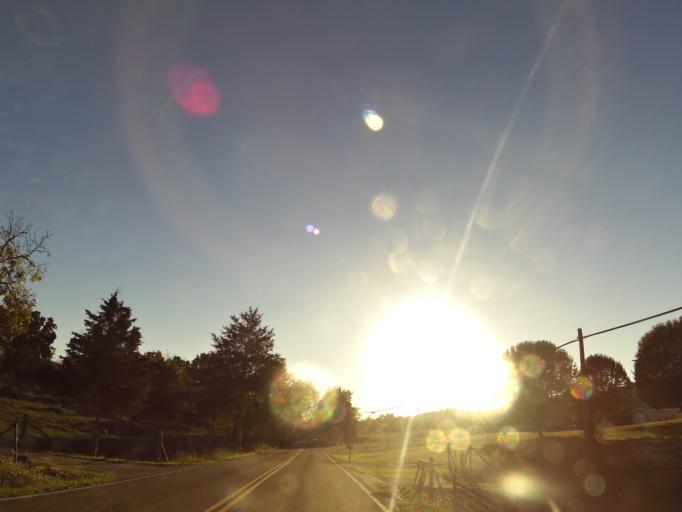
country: US
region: Tennessee
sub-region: Grainger County
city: Rutledge
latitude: 36.3276
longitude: -83.5140
